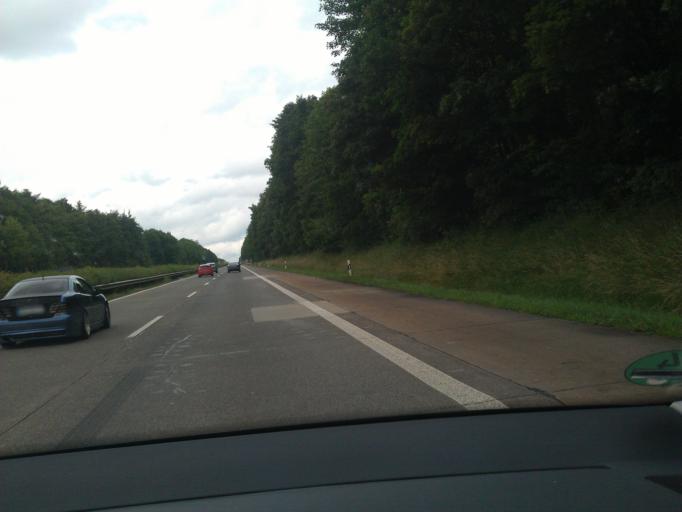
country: DE
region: Rheinland-Pfalz
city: Fohren
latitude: 49.8383
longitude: 6.7714
